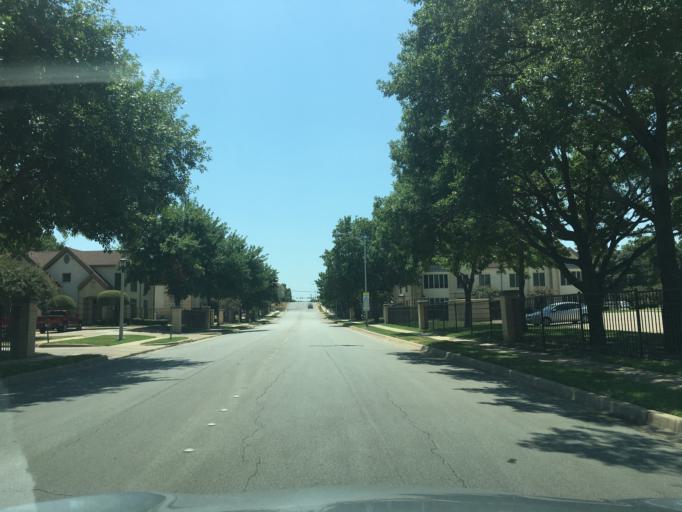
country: US
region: Texas
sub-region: Tarrant County
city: Fort Worth
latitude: 32.7095
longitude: -97.3534
